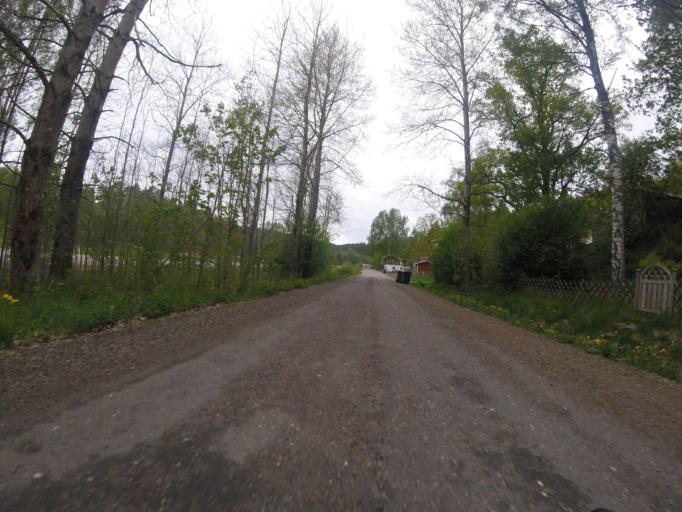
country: SE
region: Vaestra Goetaland
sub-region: Alingsas Kommun
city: Alingsas
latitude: 57.8943
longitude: 12.5506
